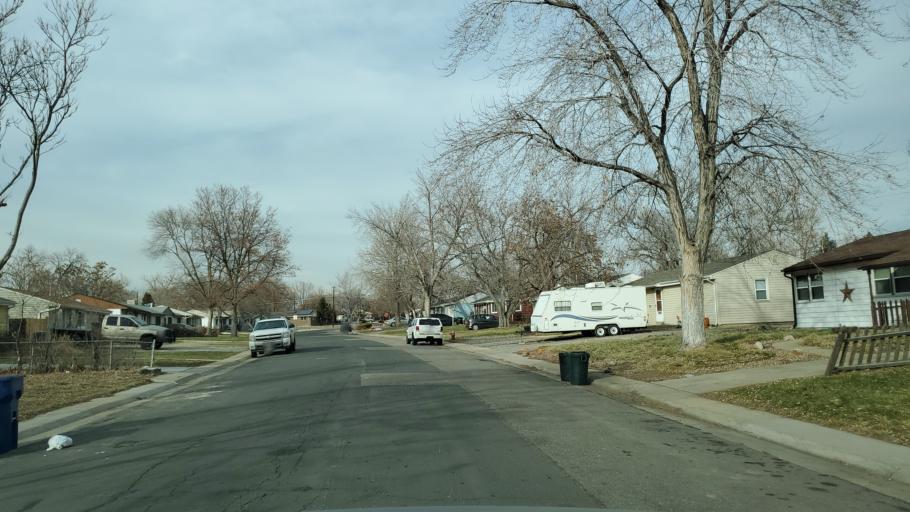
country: US
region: Colorado
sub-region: Adams County
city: Twin Lakes
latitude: 39.8295
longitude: -105.0204
